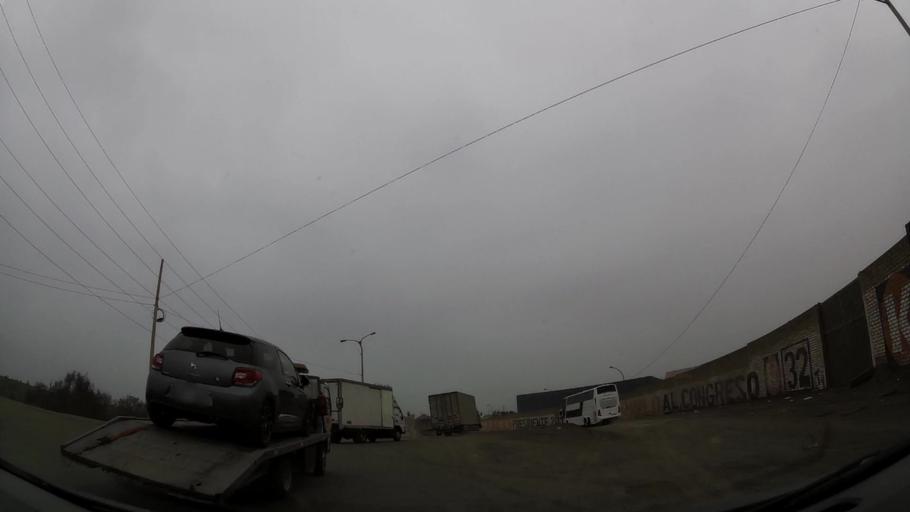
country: PE
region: Lima
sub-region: Lima
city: Punta Hermosa
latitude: -12.3002
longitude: -76.8446
